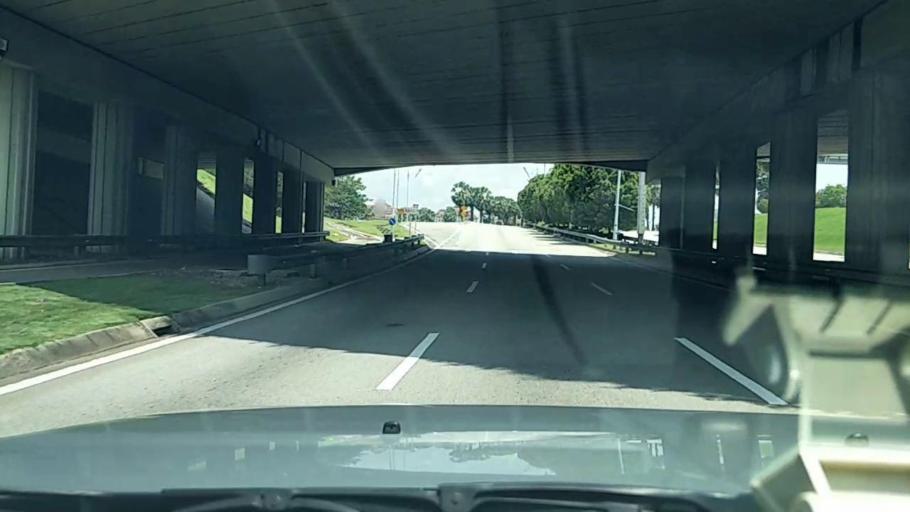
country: MY
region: Putrajaya
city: Putrajaya
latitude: 2.9523
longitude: 101.6838
